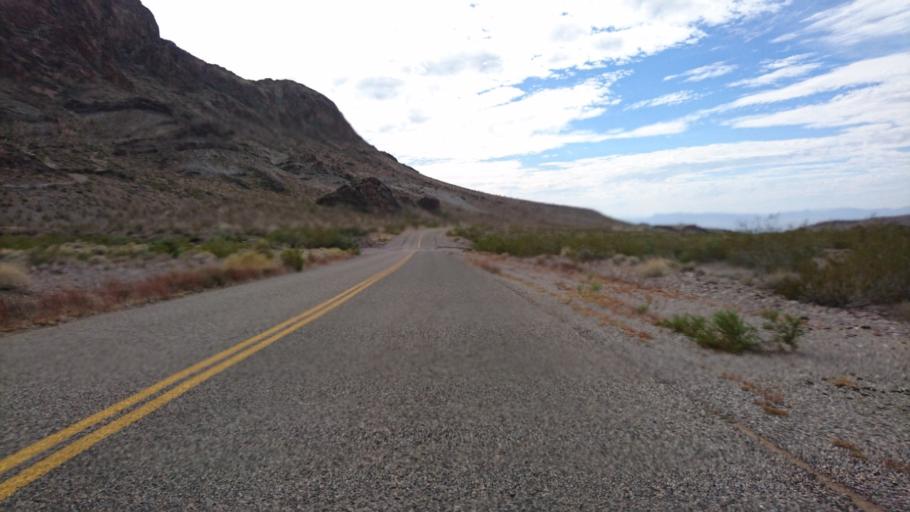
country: US
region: Arizona
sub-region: Mohave County
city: Mohave Valley
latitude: 34.9916
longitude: -114.4171
